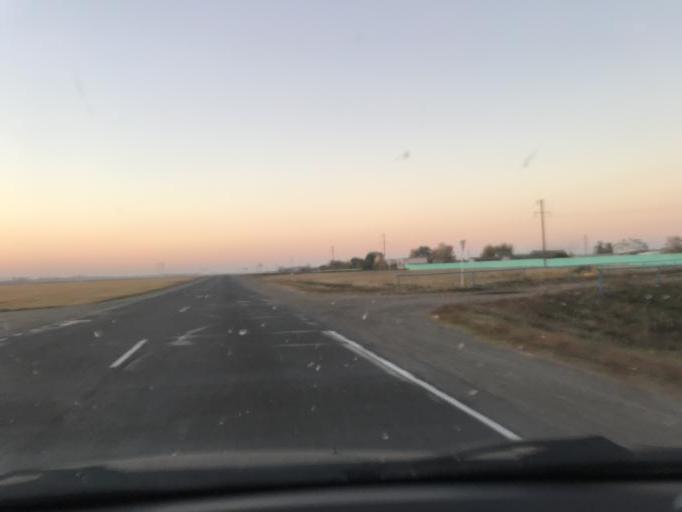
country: BY
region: Gomel
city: Horad Rechytsa
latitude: 52.2490
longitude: 30.4961
